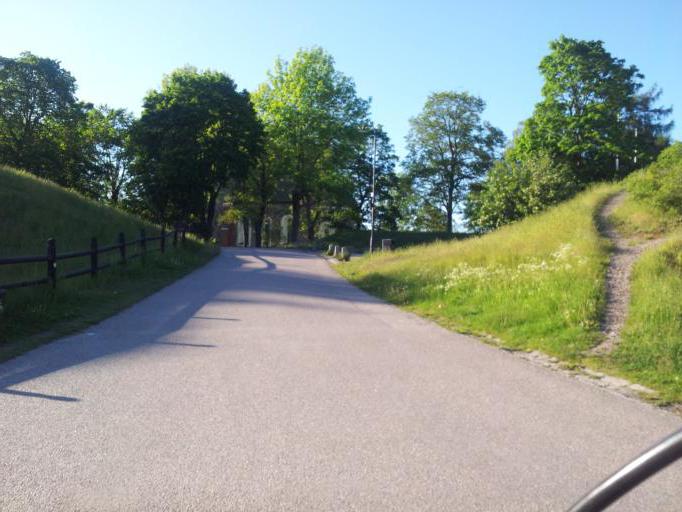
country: SE
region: Uppsala
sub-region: Uppsala Kommun
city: Gamla Uppsala
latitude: 59.8985
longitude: 17.6325
